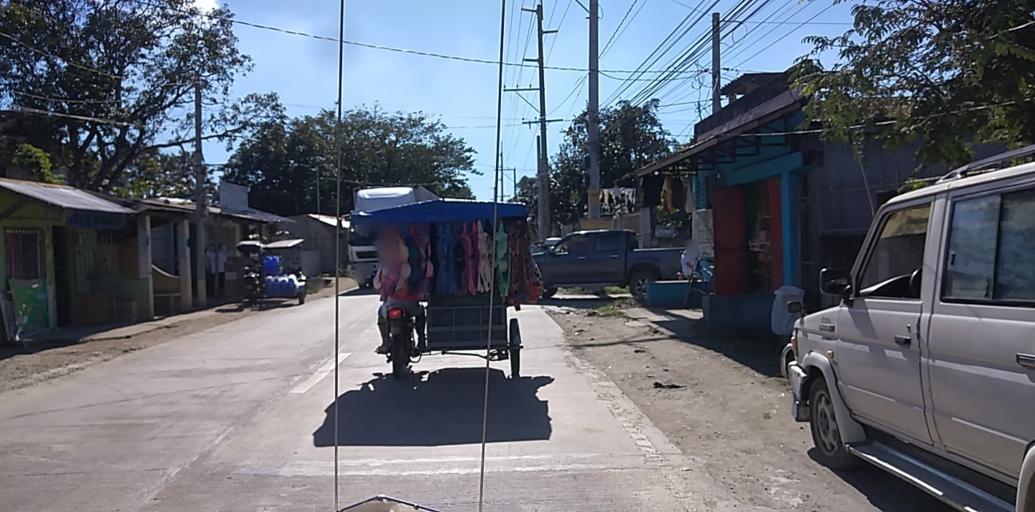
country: PH
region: Central Luzon
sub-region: Province of Pampanga
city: San Luis
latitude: 15.0561
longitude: 120.7771
